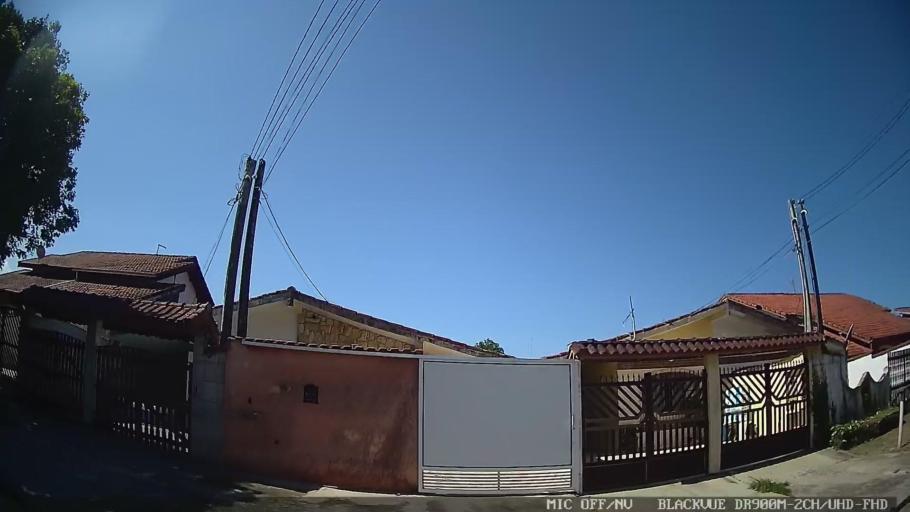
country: BR
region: Sao Paulo
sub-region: Peruibe
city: Peruibe
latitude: -24.3114
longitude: -46.9979
